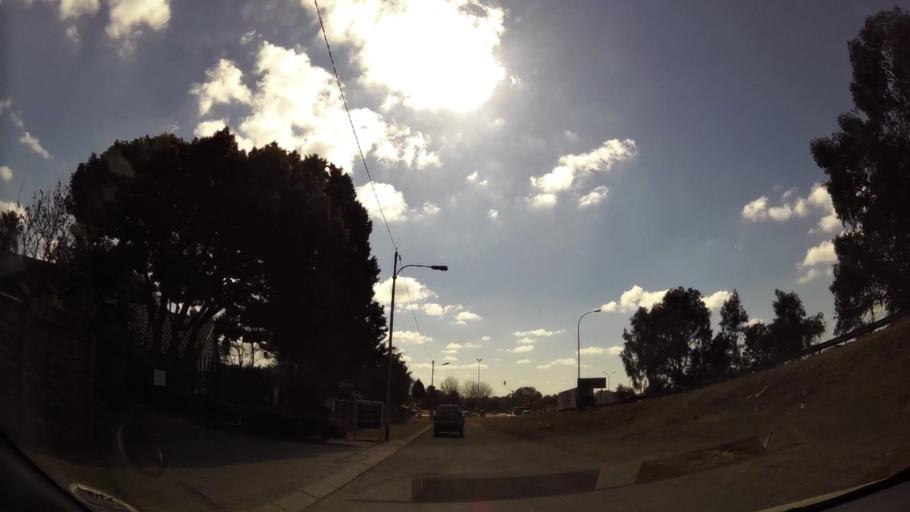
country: ZA
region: Gauteng
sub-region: City of Johannesburg Metropolitan Municipality
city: Roodepoort
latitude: -26.1279
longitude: 27.8393
